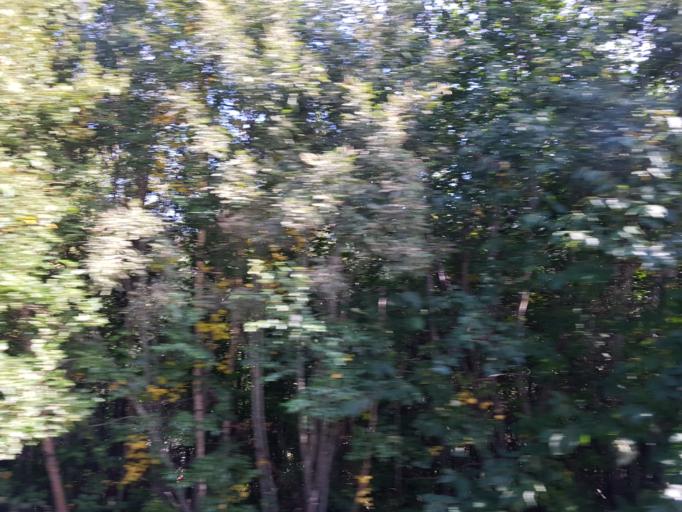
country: NO
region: Sor-Trondelag
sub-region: Afjord
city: Arnes
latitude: 63.9684
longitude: 10.2236
